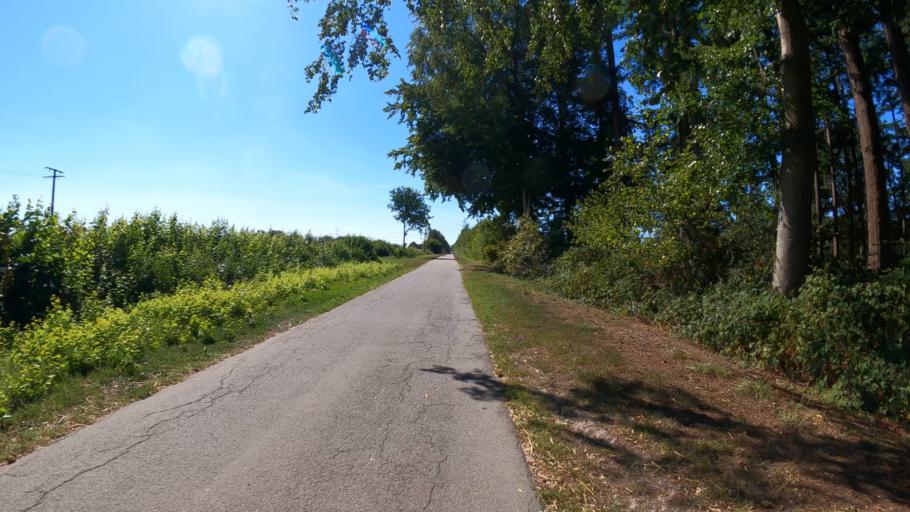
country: DE
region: Schleswig-Holstein
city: Hohenhorn
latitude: 53.4769
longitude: 10.3516
